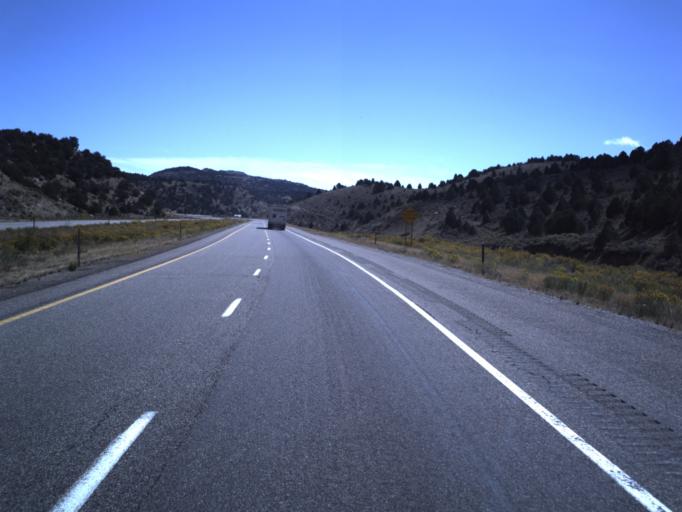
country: US
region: Utah
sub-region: Sevier County
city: Salina
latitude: 38.8047
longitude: -111.5278
